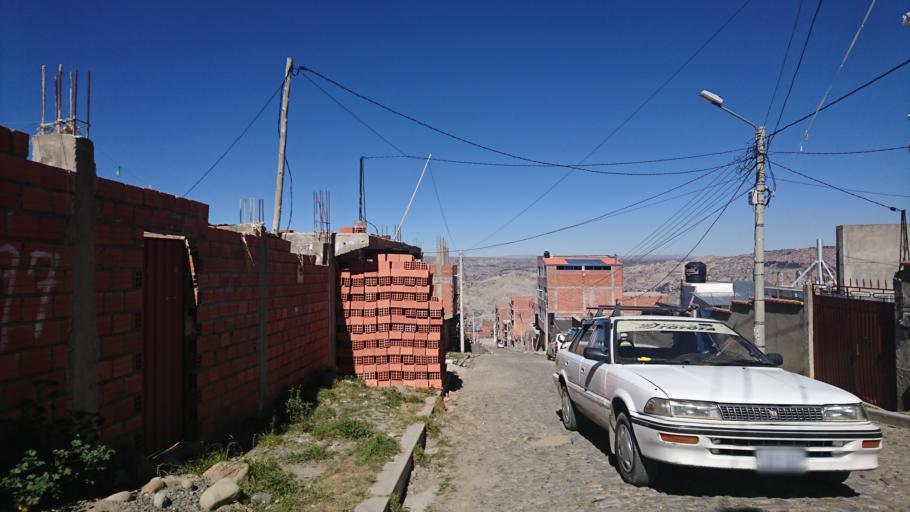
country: BO
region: La Paz
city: La Paz
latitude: -16.4875
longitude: -68.1031
